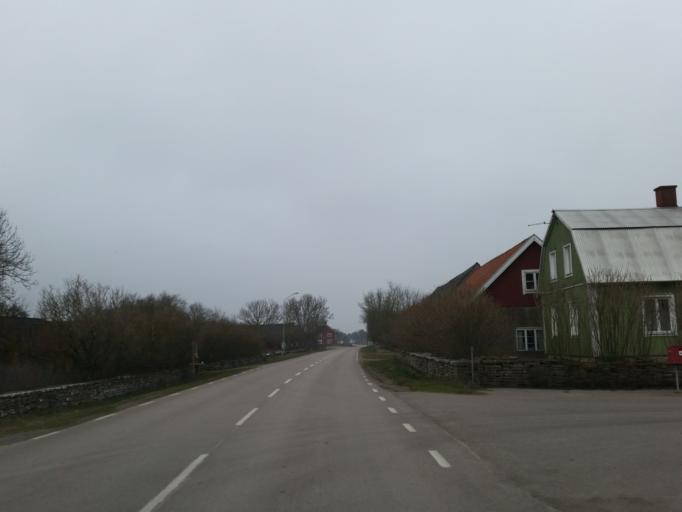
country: SE
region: Kalmar
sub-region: Morbylanga Kommun
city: Sodra Sandby
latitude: 56.4820
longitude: 16.5749
